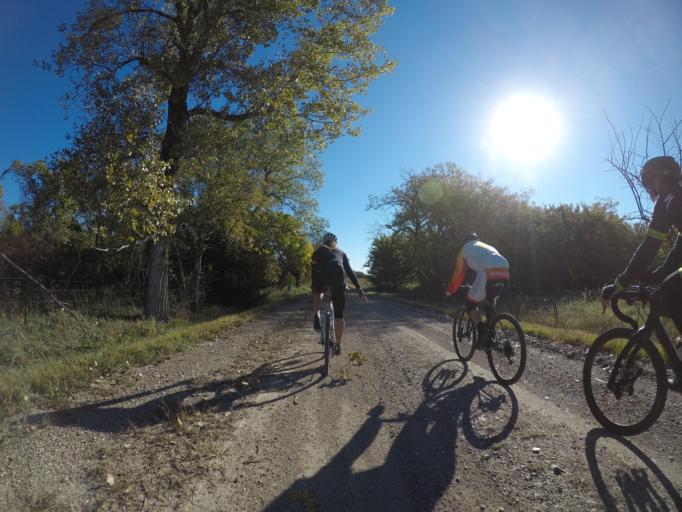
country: US
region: Kansas
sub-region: Morris County
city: Council Grove
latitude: 38.8256
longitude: -96.4309
